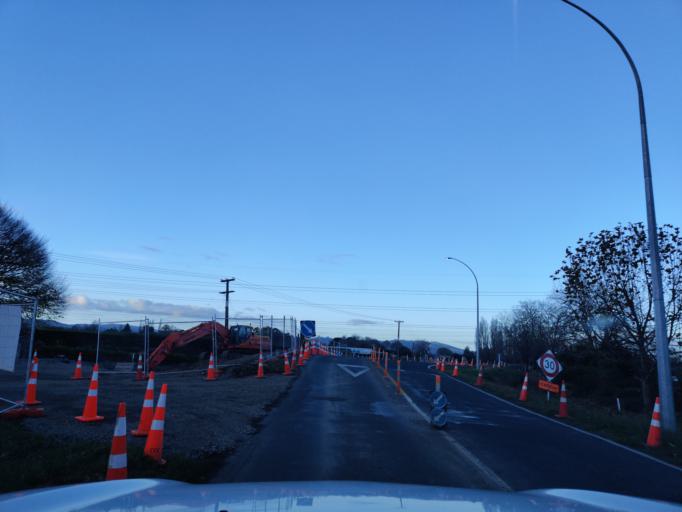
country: NZ
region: Waikato
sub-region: Waipa District
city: Cambridge
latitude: -37.8892
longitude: 175.4340
